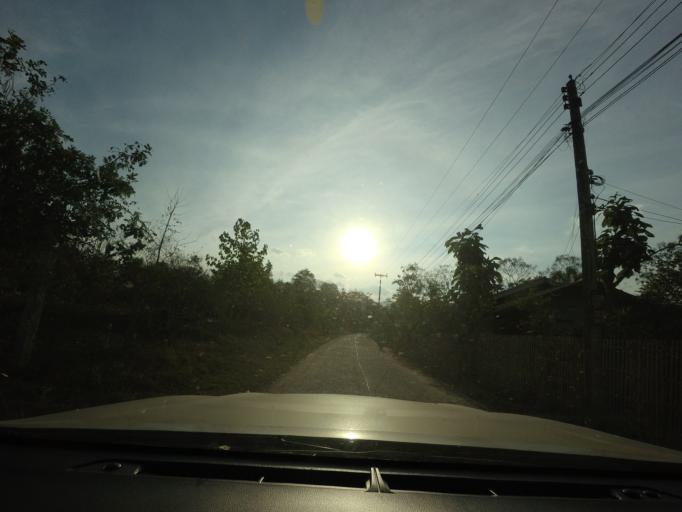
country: TH
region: Mae Hong Son
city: Mae Hi
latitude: 19.3418
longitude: 98.4313
